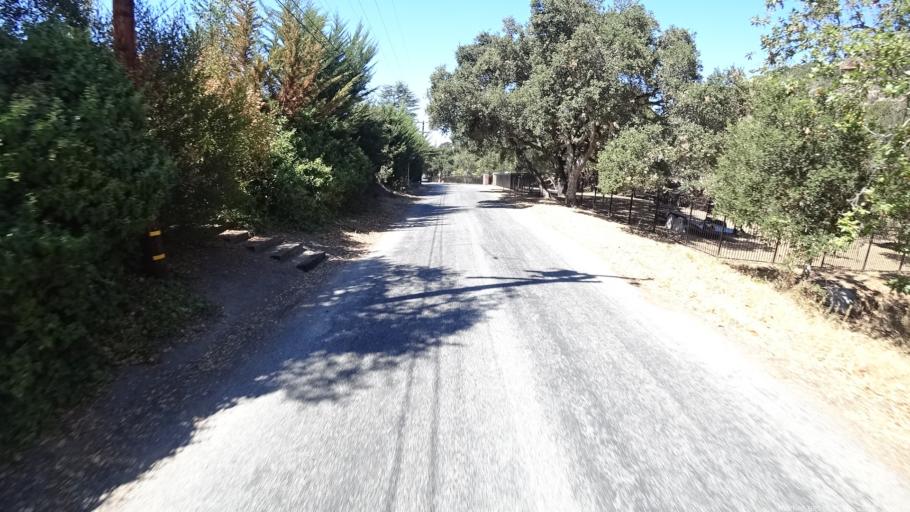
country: US
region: California
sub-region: Monterey County
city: Carmel Valley Village
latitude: 36.5658
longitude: -121.6982
